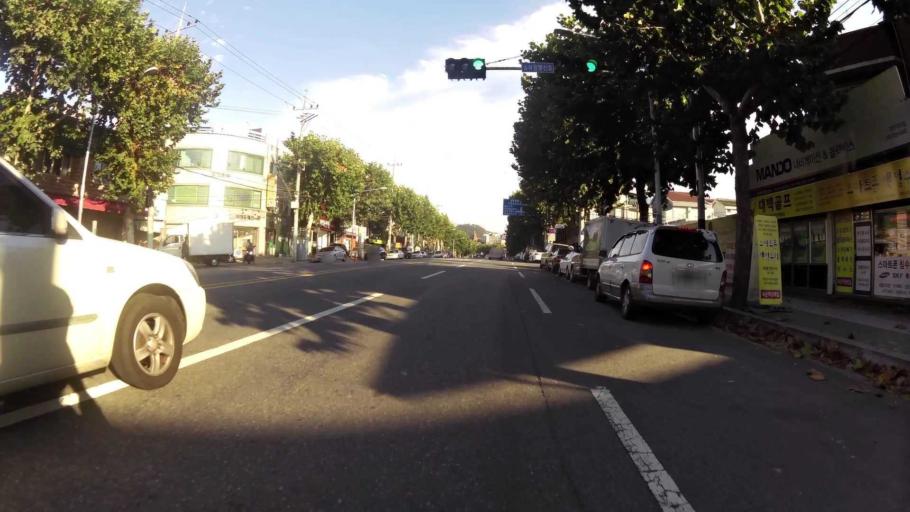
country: KR
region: Daegu
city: Daegu
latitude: 35.8671
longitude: 128.6364
